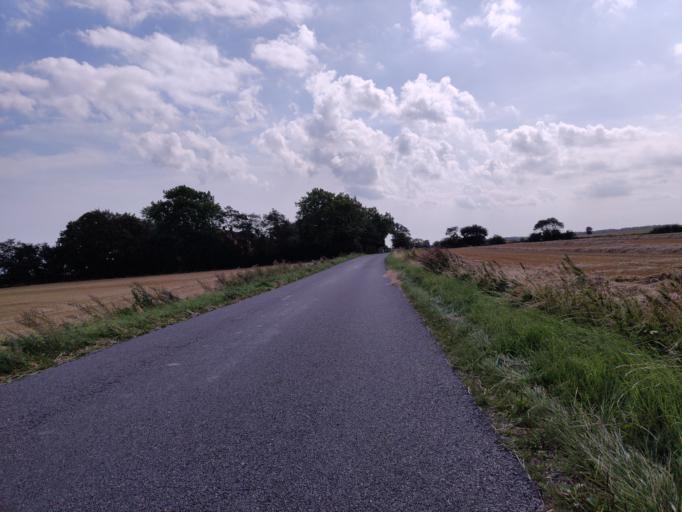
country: DK
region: Zealand
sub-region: Guldborgsund Kommune
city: Nykobing Falster
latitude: 54.6651
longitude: 11.8907
